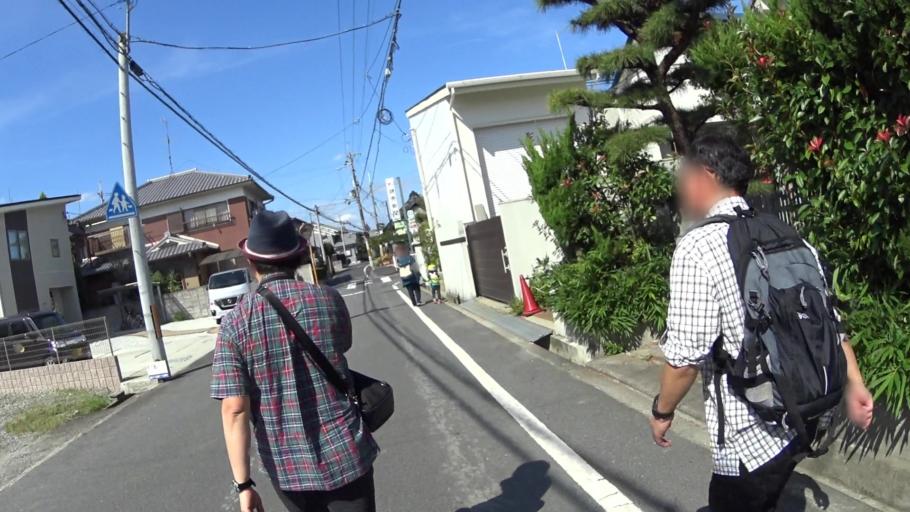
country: JP
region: Nara
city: Sakurai
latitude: 34.5318
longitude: 135.8418
